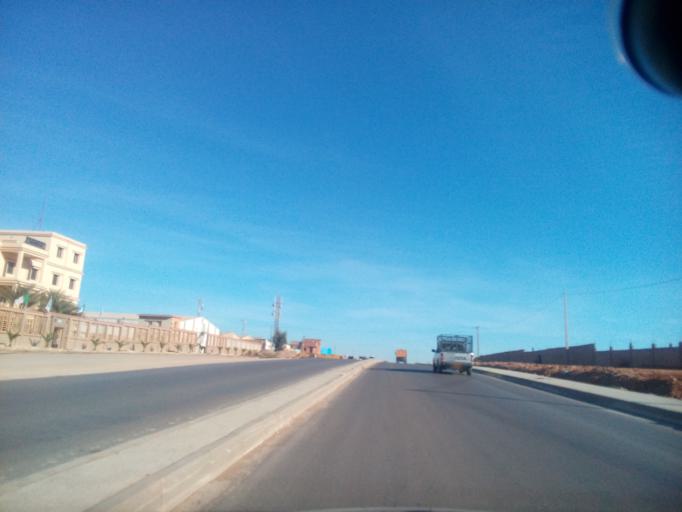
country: DZ
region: Mostaganem
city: Mostaganem
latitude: 35.9119
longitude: 0.1458
